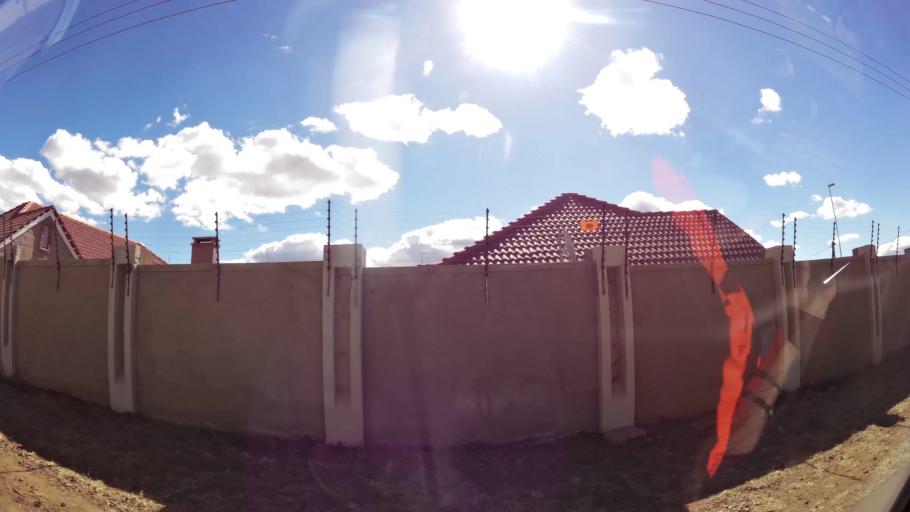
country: ZA
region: Limpopo
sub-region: Capricorn District Municipality
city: Polokwane
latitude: -23.8790
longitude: 29.5153
